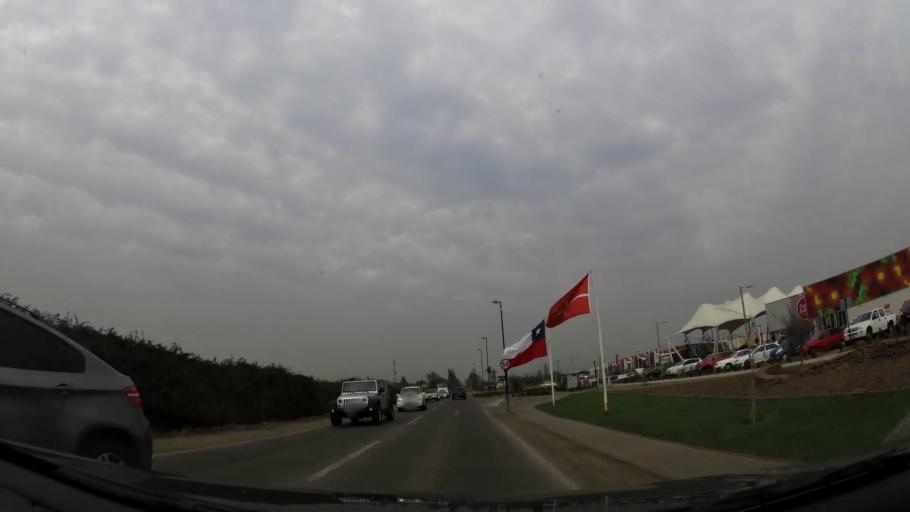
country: CL
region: Santiago Metropolitan
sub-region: Provincia de Chacabuco
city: Chicureo Abajo
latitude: -33.2891
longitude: -70.7012
